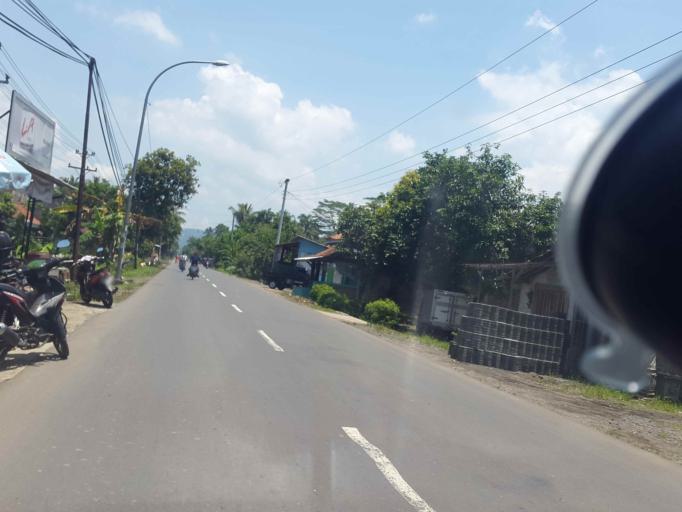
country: ID
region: Central Java
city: Klapagading
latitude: -7.5181
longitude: 109.0721
